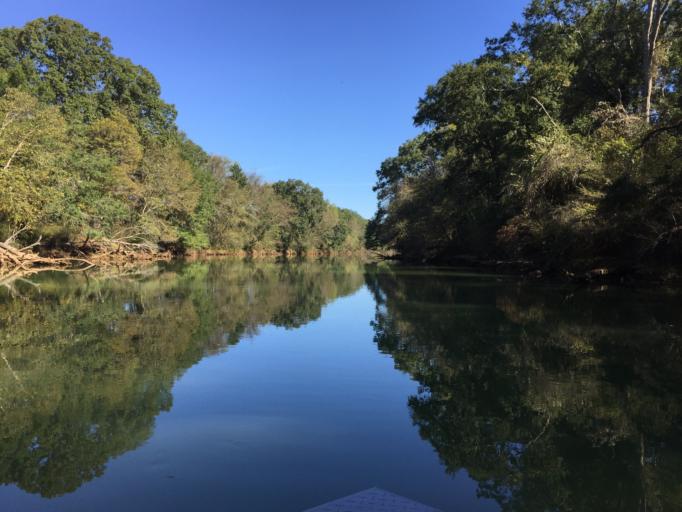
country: US
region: Georgia
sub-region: Fulton County
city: Johns Creek
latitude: 34.0223
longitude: -84.1743
